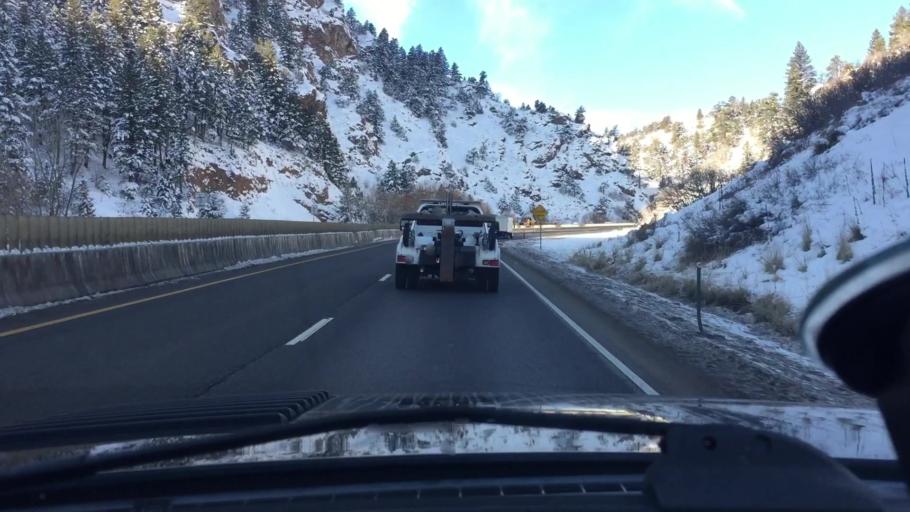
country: US
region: Colorado
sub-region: Jefferson County
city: Indian Hills
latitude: 39.6179
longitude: -105.2161
